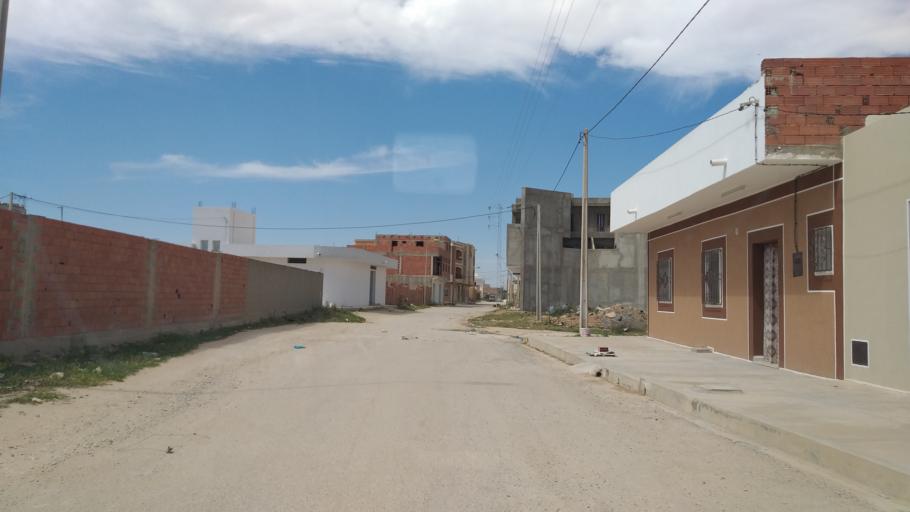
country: TN
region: Al Mahdiyah
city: El Jem
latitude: 35.3019
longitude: 10.6984
